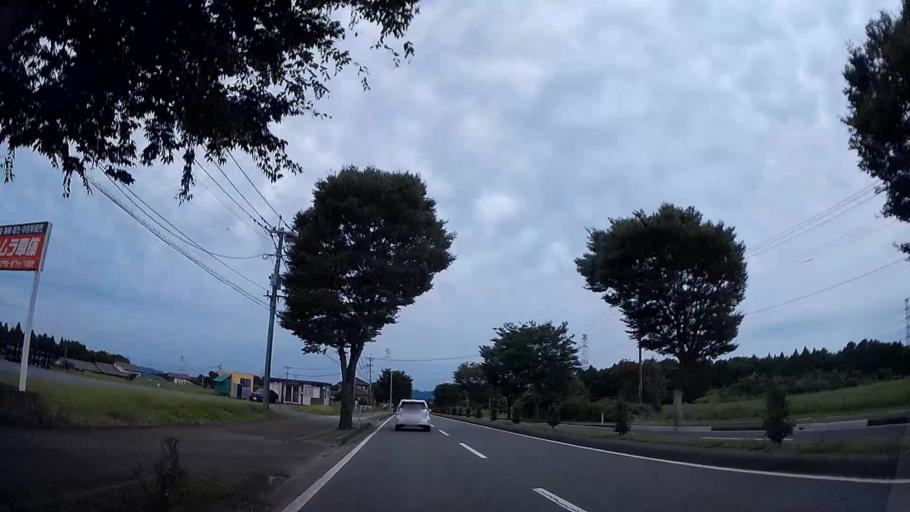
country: JP
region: Kumamoto
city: Ozu
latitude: 32.9138
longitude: 130.8414
